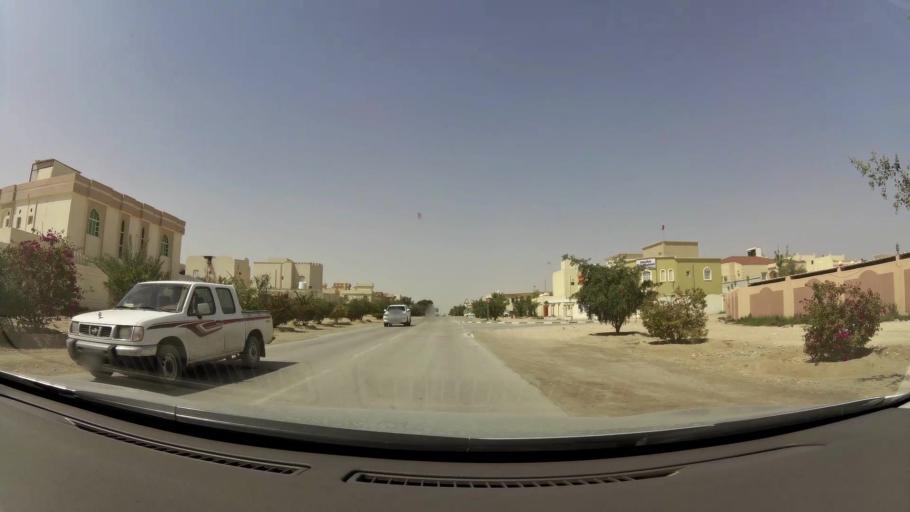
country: QA
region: Baladiyat Umm Salal
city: Umm Salal Muhammad
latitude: 25.3787
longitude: 51.4198
